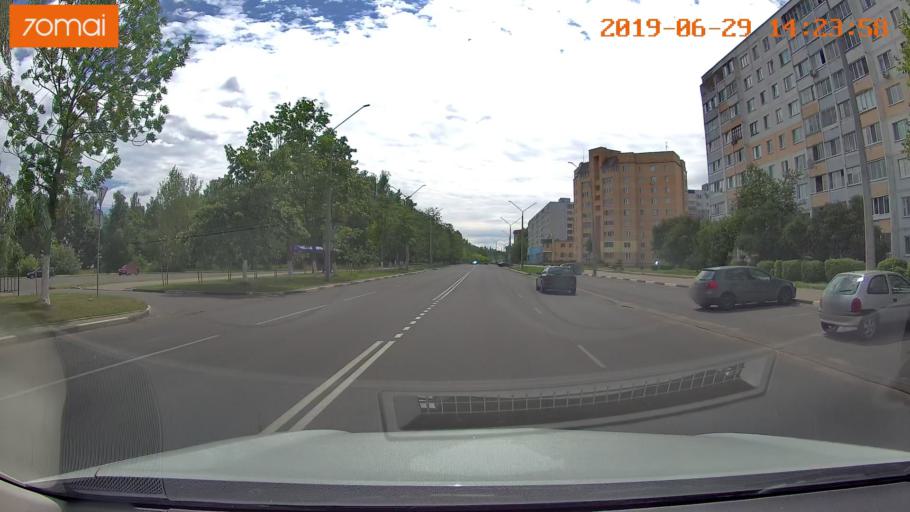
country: BY
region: Minsk
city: Salihorsk
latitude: 52.7831
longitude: 27.5521
